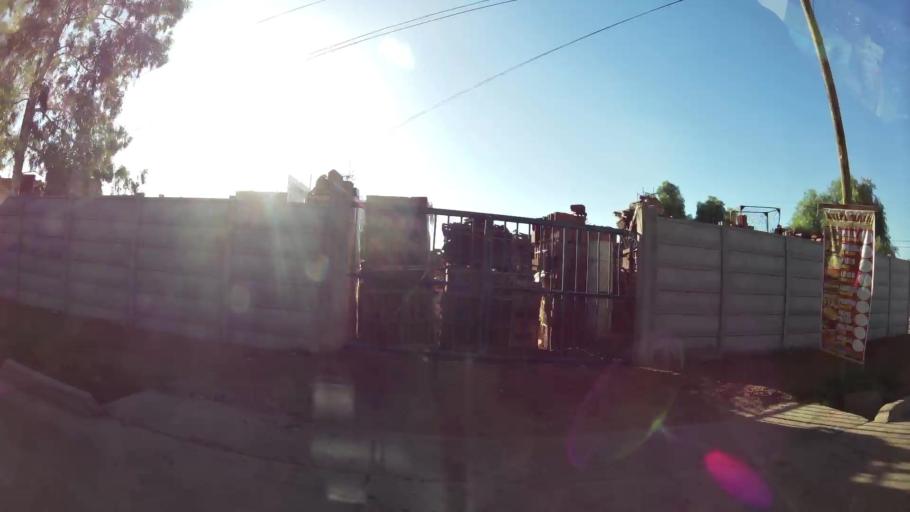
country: AR
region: Mendoza
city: Mendoza
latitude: -32.8732
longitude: -68.8203
